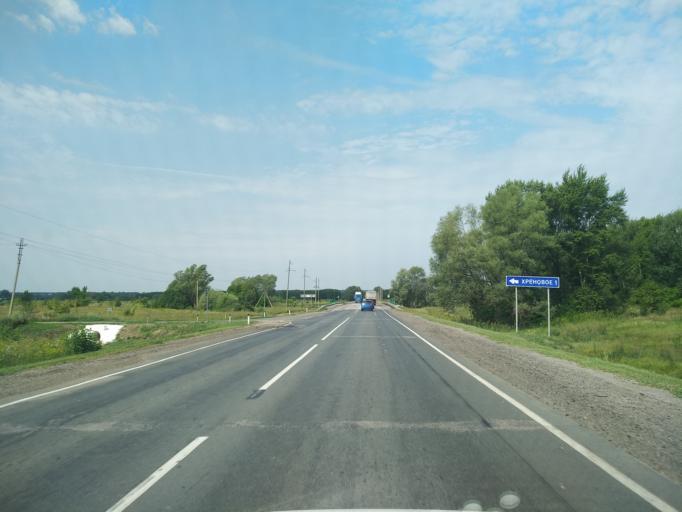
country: RU
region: Voronezj
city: Orlovo
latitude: 51.6803
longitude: 39.6120
